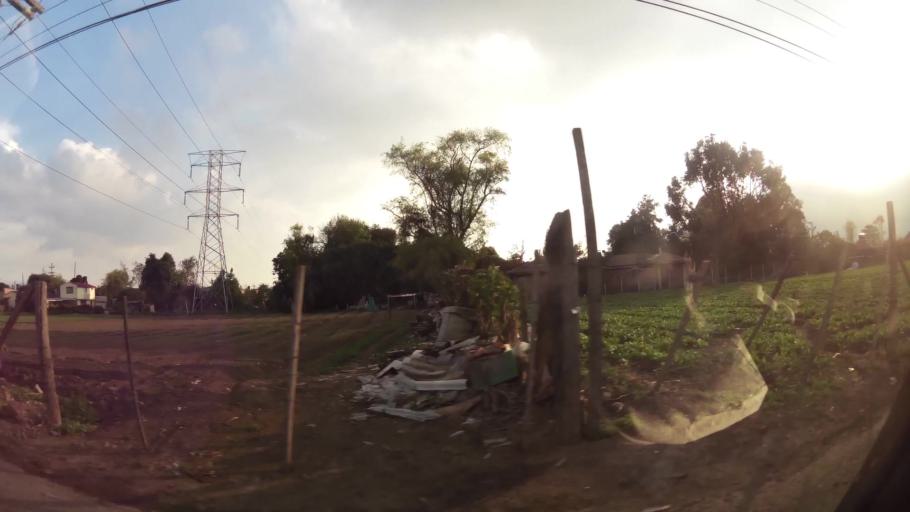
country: CO
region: Cundinamarca
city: Cota
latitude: 4.8208
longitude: -74.0947
